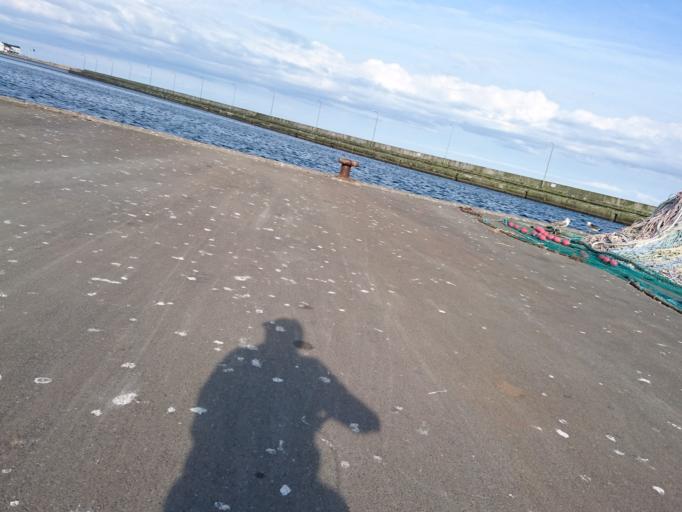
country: DK
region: North Denmark
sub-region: Frederikshavn Kommune
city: Skagen
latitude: 57.7167
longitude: 10.5957
